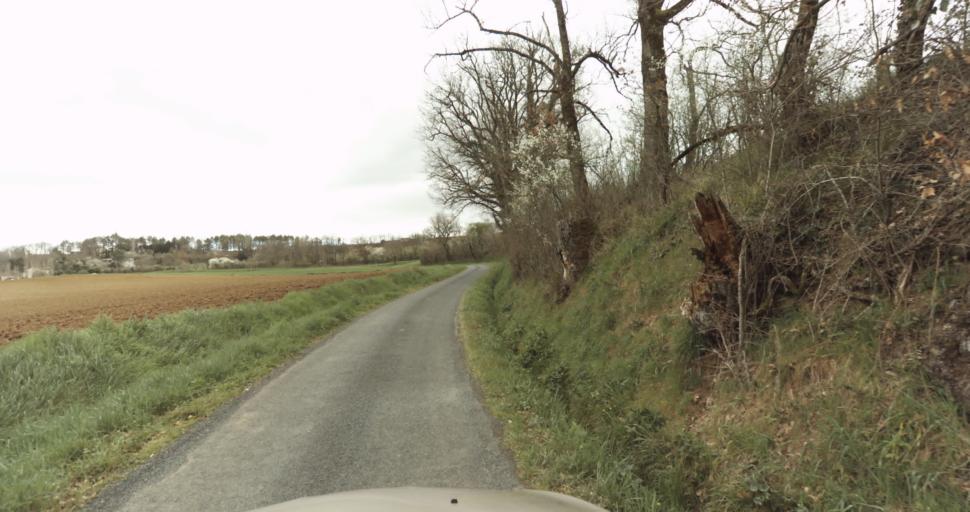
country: FR
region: Midi-Pyrenees
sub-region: Departement du Tarn
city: Puygouzon
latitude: 43.8725
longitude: 2.1730
